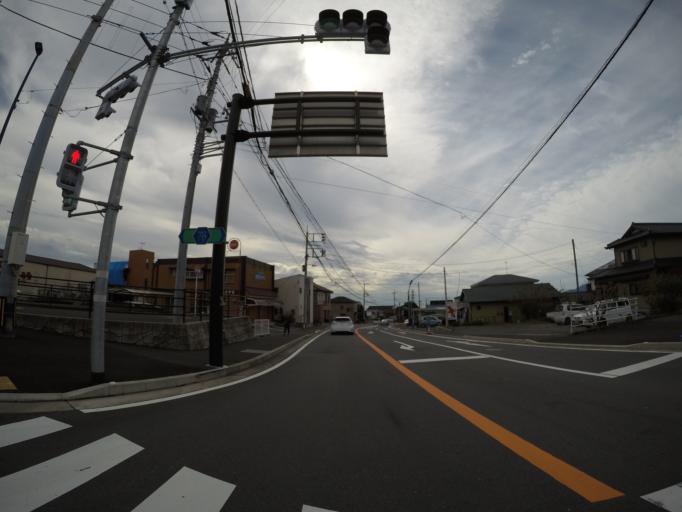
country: JP
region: Shizuoka
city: Fuji
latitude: 35.2107
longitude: 138.6866
